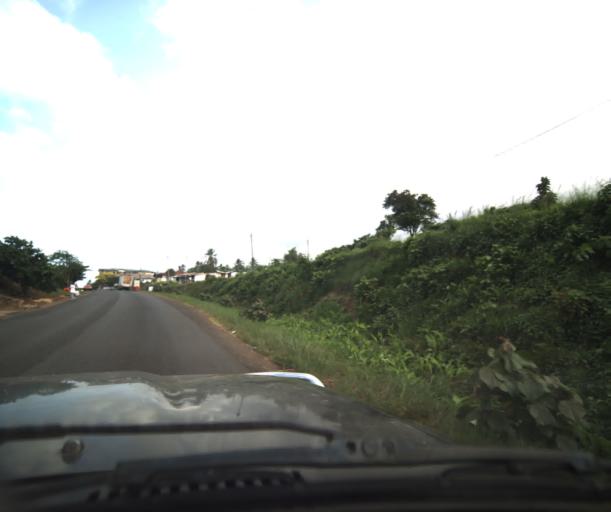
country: CM
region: South-West Province
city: Limbe
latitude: 4.0188
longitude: 9.1380
